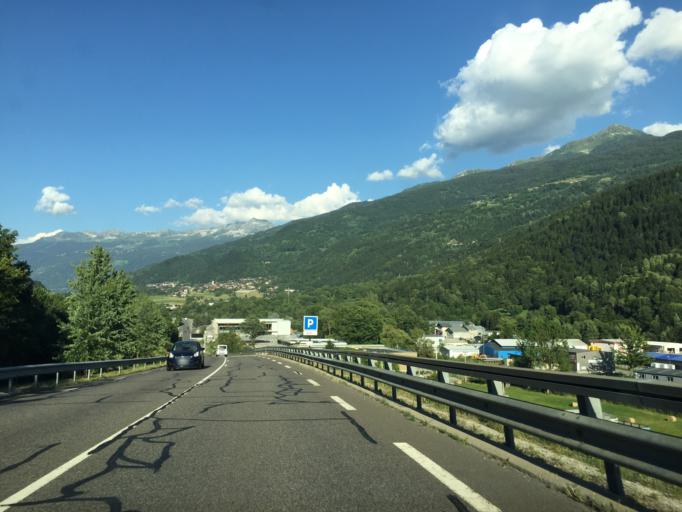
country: FR
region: Rhone-Alpes
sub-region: Departement de la Savoie
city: Aime
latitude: 45.5531
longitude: 6.6402
